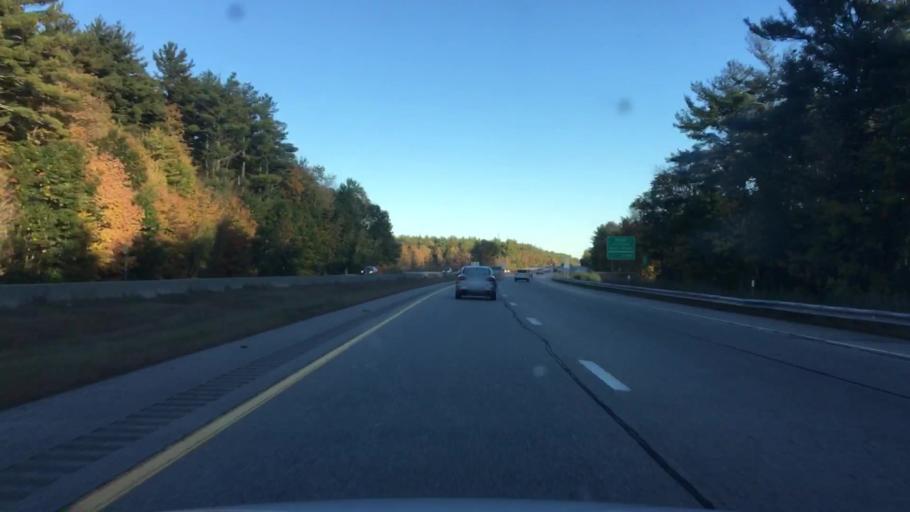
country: US
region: New Hampshire
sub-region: Rockingham County
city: Epping
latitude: 43.0252
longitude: -71.0663
